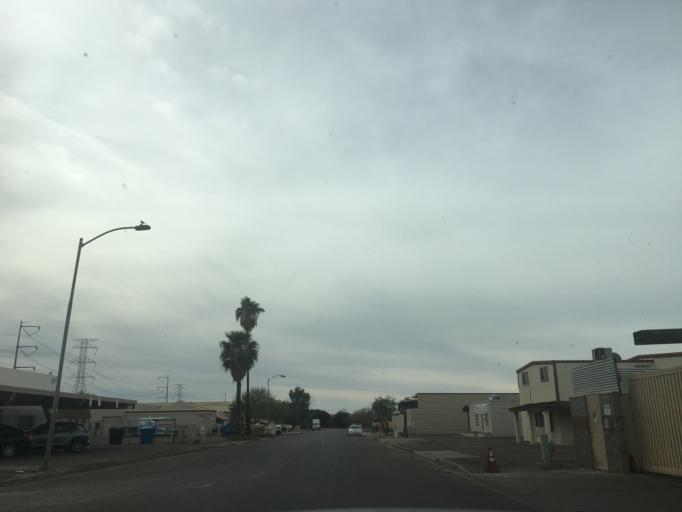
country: US
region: Arizona
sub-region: Maricopa County
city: Gilbert
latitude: 33.3583
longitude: -111.8041
